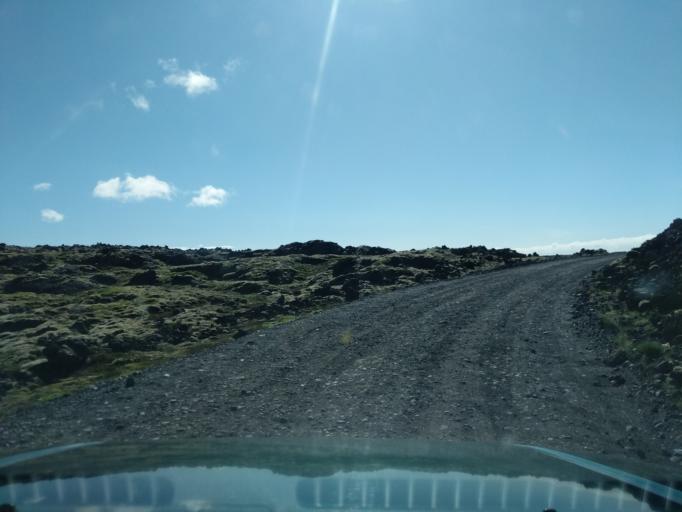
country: IS
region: West
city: Olafsvik
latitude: 64.8739
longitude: -24.0108
